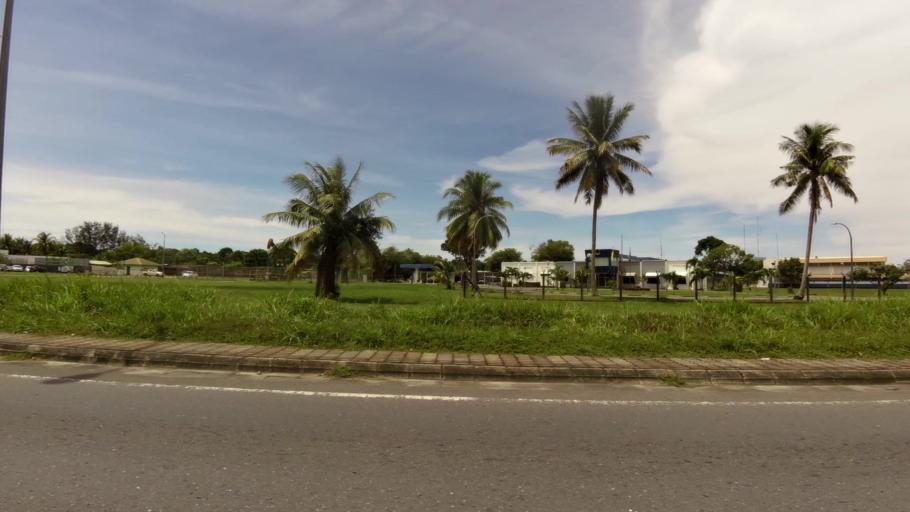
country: BN
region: Belait
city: Seria
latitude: 4.6007
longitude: 114.2855
